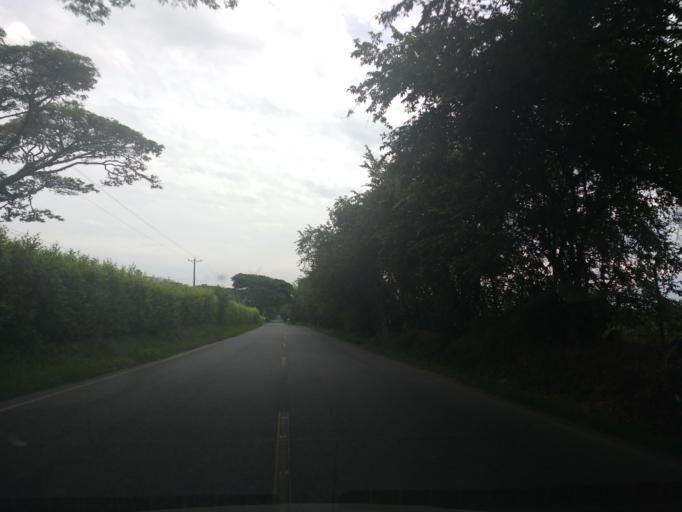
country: CO
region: Valle del Cauca
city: Florida
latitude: 3.3036
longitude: -76.2327
